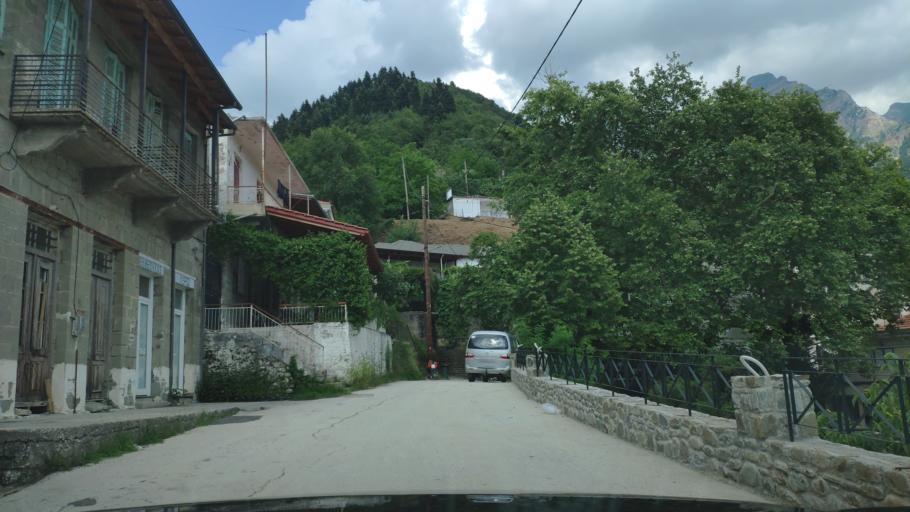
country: GR
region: Epirus
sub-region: Nomos Ioanninon
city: Pramanta
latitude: 39.4741
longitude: 21.0799
